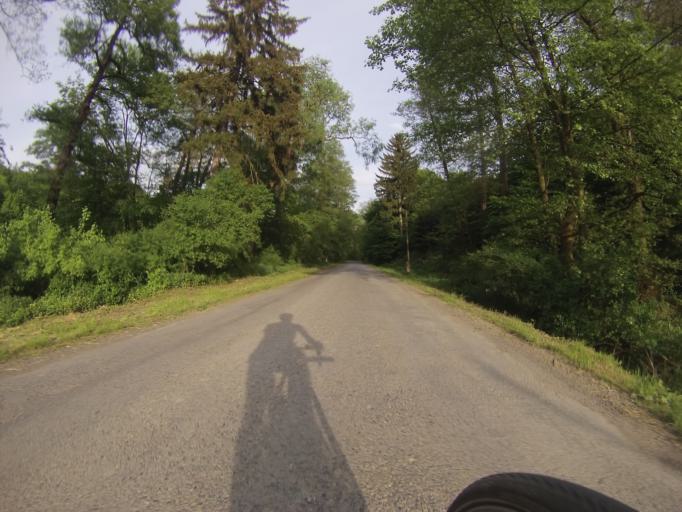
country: CZ
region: Olomoucky
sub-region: Okres Prostejov
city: Plumlov
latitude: 49.4676
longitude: 16.9732
